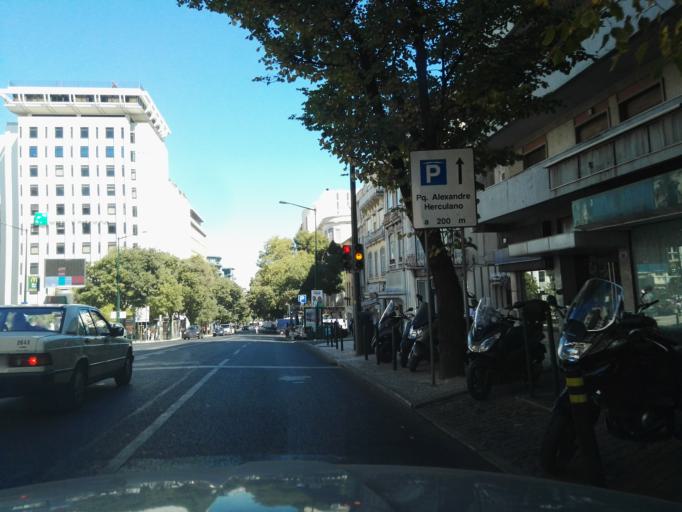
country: PT
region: Lisbon
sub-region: Lisbon
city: Lisbon
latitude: 38.7209
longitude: -9.1527
